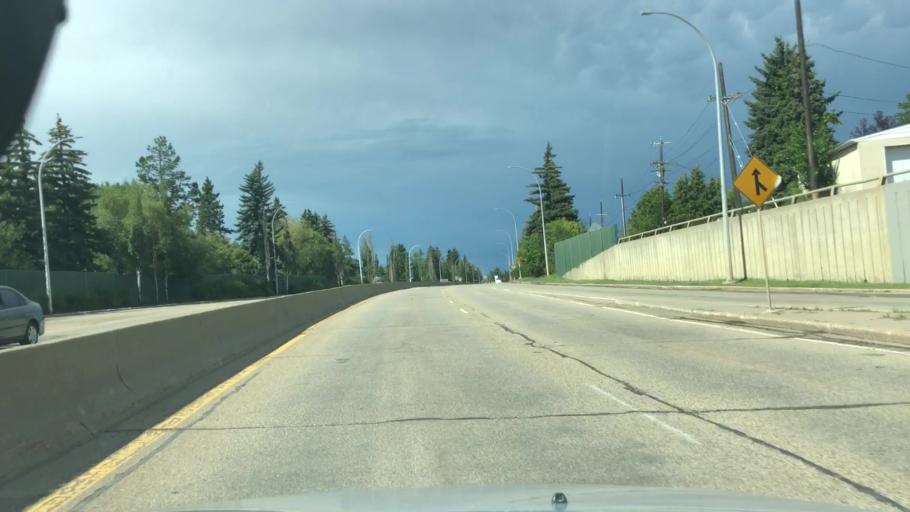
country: CA
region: Alberta
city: Edmonton
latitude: 53.5528
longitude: -113.5506
